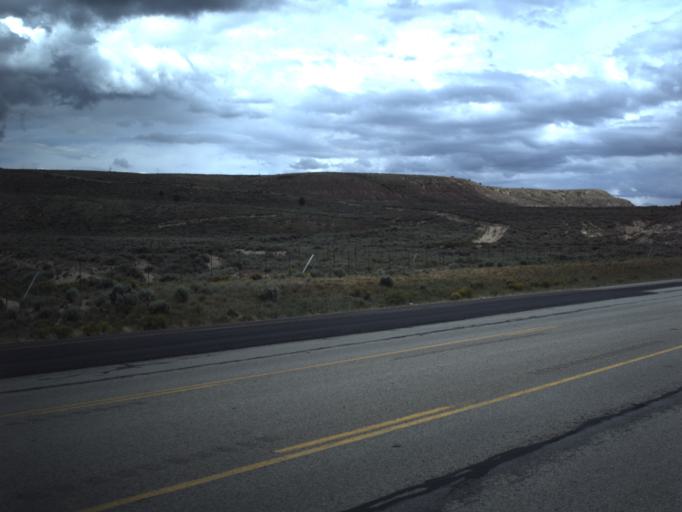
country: US
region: Utah
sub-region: Carbon County
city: Helper
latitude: 39.8536
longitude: -111.0150
